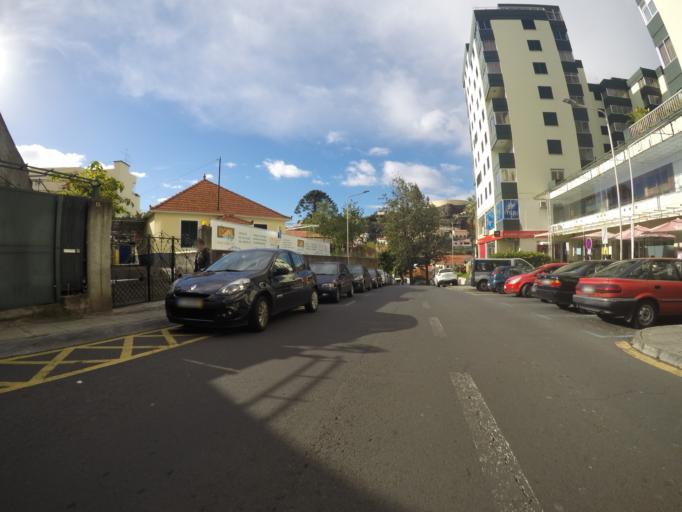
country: PT
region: Madeira
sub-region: Funchal
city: Nossa Senhora do Monte
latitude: 32.6565
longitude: -16.9140
